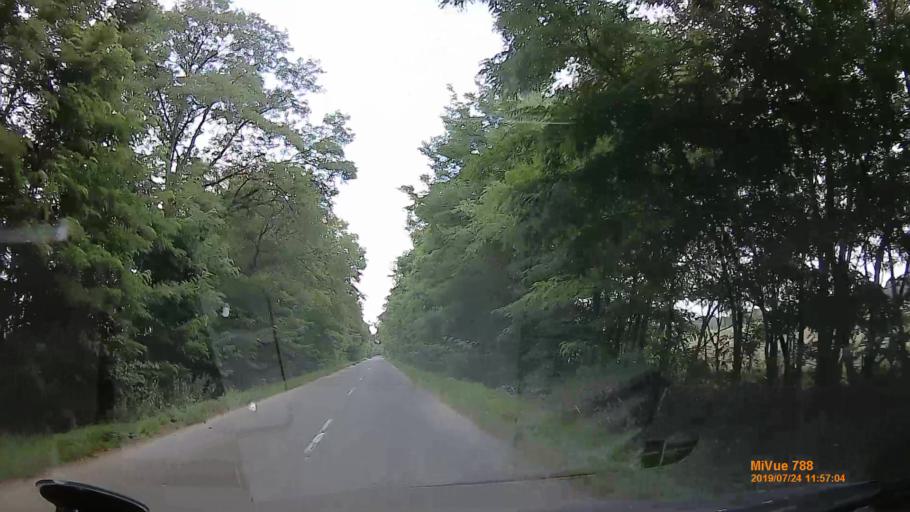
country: HU
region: Szabolcs-Szatmar-Bereg
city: Vasarosnameny
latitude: 48.2024
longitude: 22.4235
